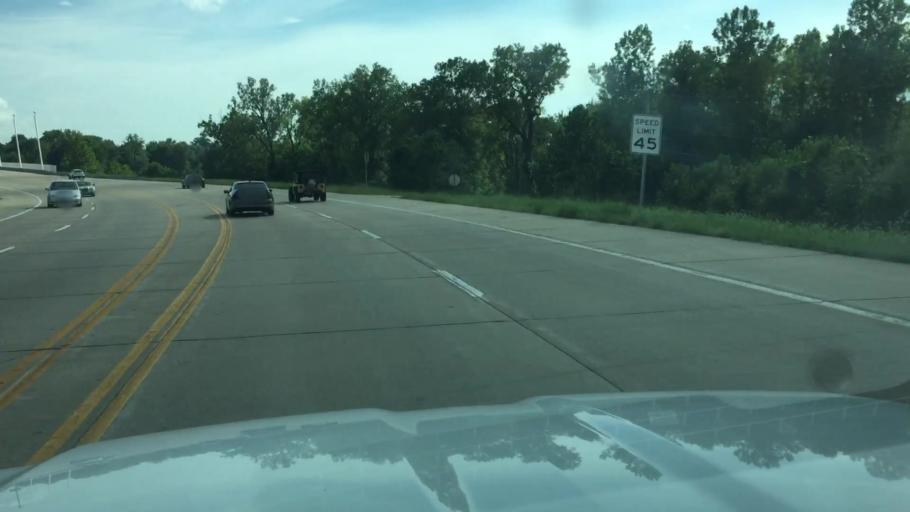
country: US
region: Missouri
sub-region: Jefferson County
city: Arnold
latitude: 38.4598
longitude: -90.3601
